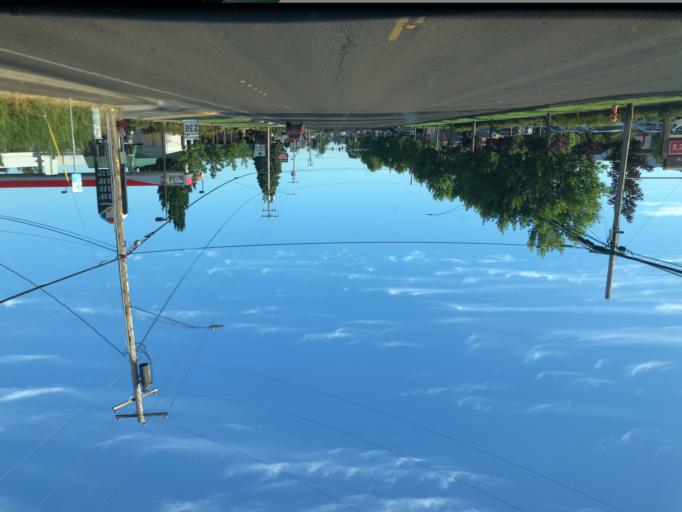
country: US
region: Oregon
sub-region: Benton County
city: Corvallis
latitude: 44.5812
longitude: -123.2591
